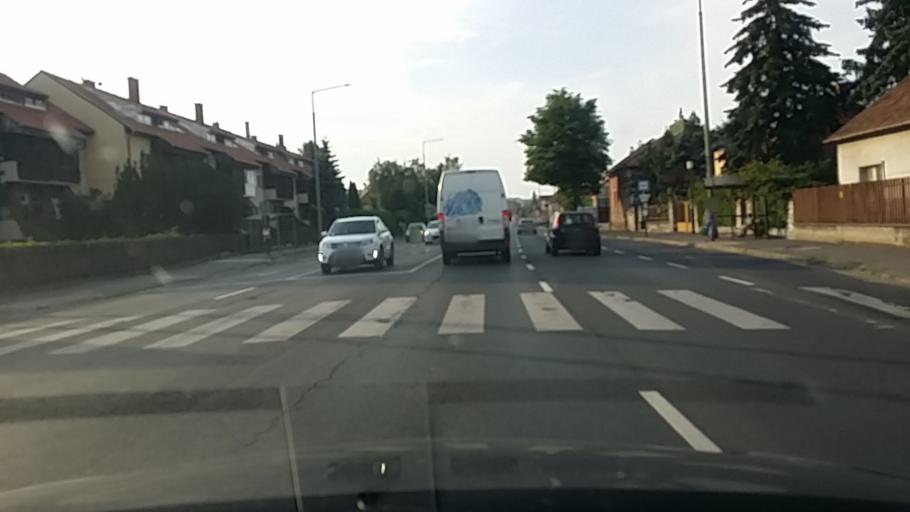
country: HU
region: Borsod-Abauj-Zemplen
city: Miskolc
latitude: 48.0673
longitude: 20.7919
